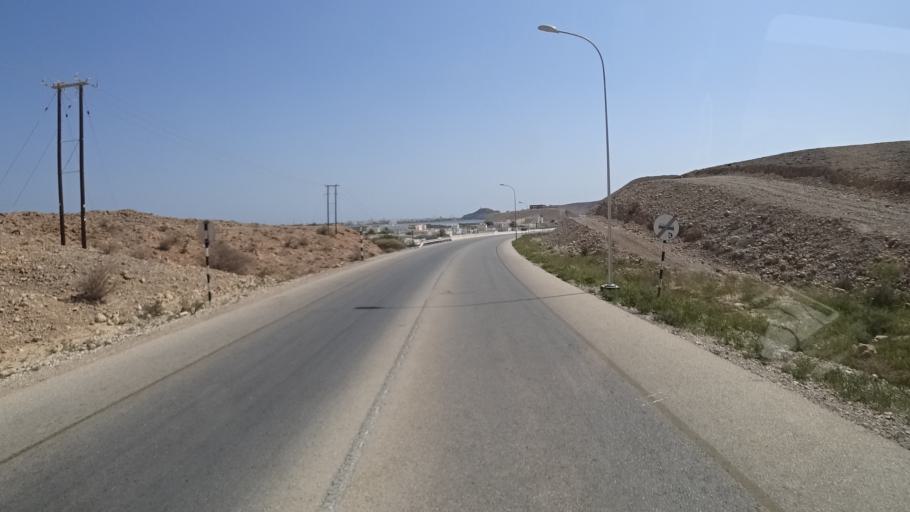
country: OM
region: Ash Sharqiyah
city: Sur
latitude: 22.5468
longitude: 59.5214
